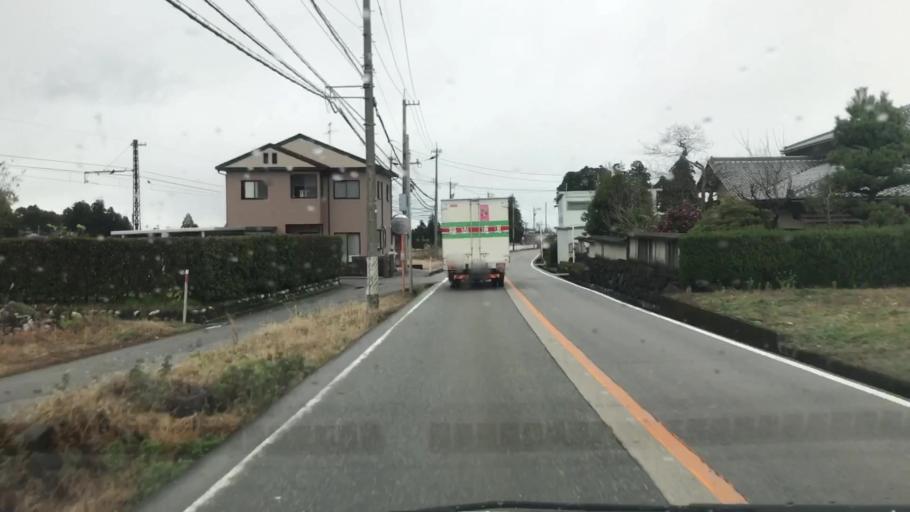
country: JP
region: Toyama
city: Kamiichi
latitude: 36.6022
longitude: 137.3214
